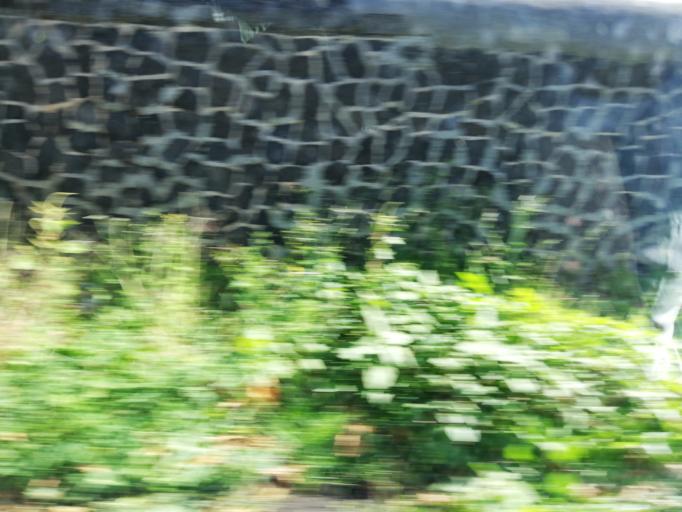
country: MU
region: Port Louis
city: Port Louis
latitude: -20.1601
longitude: 57.4879
